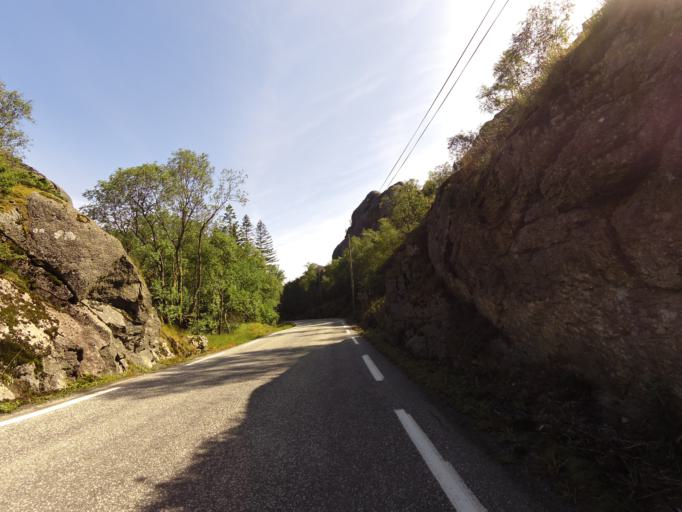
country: NO
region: Rogaland
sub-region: Sokndal
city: Hauge i Dalane
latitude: 58.3346
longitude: 6.3490
